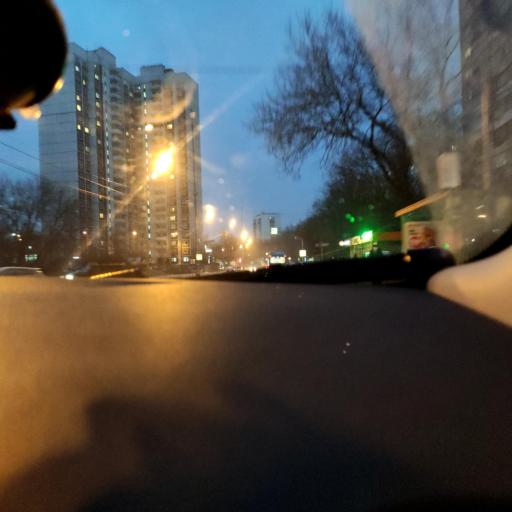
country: RU
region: Moscow
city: Vatutino
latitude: 55.8728
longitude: 37.6771
